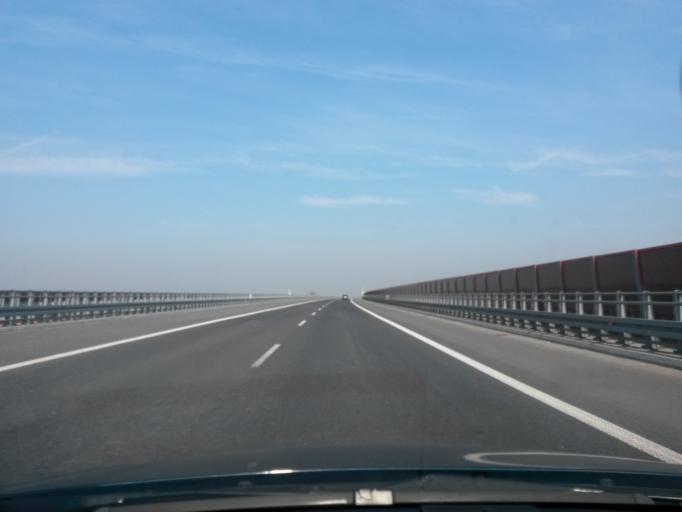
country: PL
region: Lodz Voivodeship
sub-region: Powiat kutnowski
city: Krzyzanow
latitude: 52.1319
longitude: 19.4891
